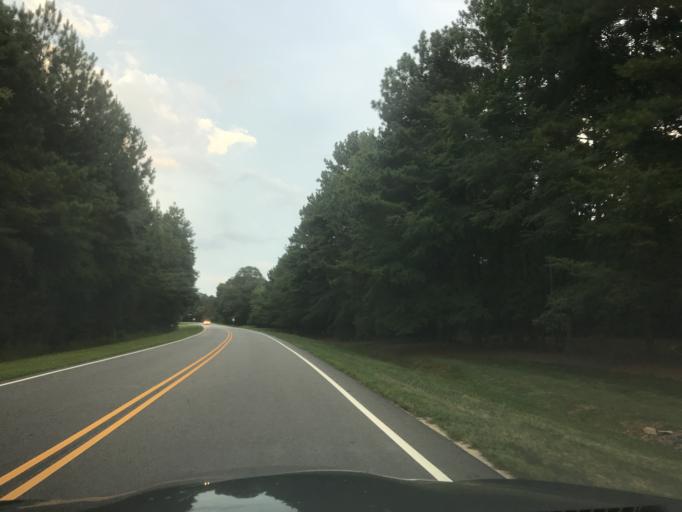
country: US
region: North Carolina
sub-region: Wake County
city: Wake Forest
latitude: 35.9201
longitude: -78.6013
